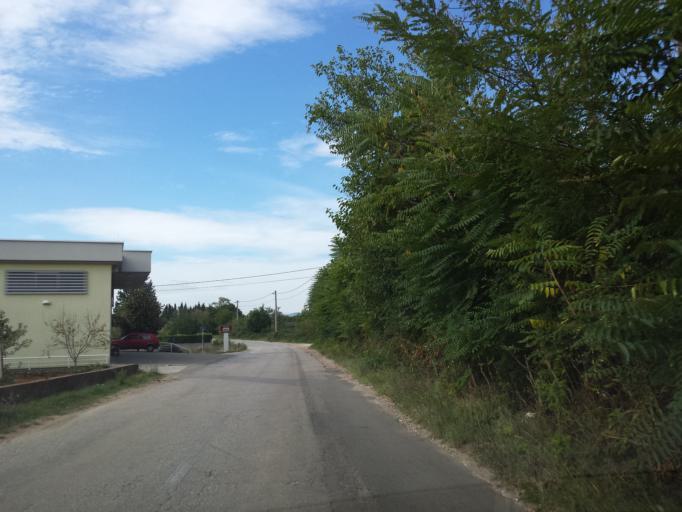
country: BA
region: Federation of Bosnia and Herzegovina
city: Citluk
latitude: 43.1940
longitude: 17.6559
